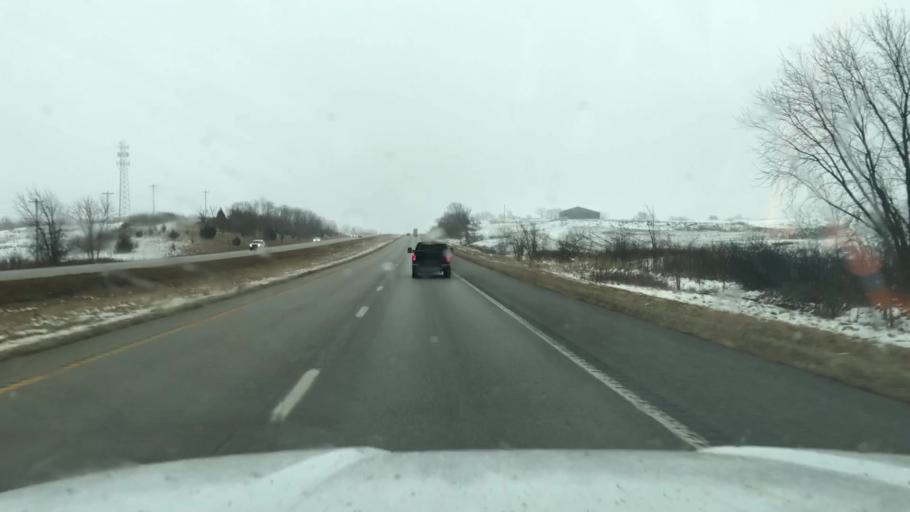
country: US
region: Missouri
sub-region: Clinton County
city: Gower
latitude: 39.7473
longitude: -94.6557
